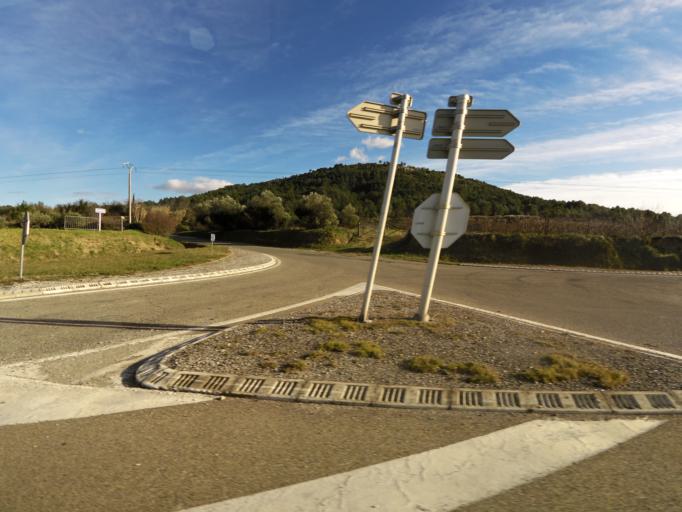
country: FR
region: Languedoc-Roussillon
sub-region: Departement du Gard
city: Nages-et-Solorgues
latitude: 43.8021
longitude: 4.2169
